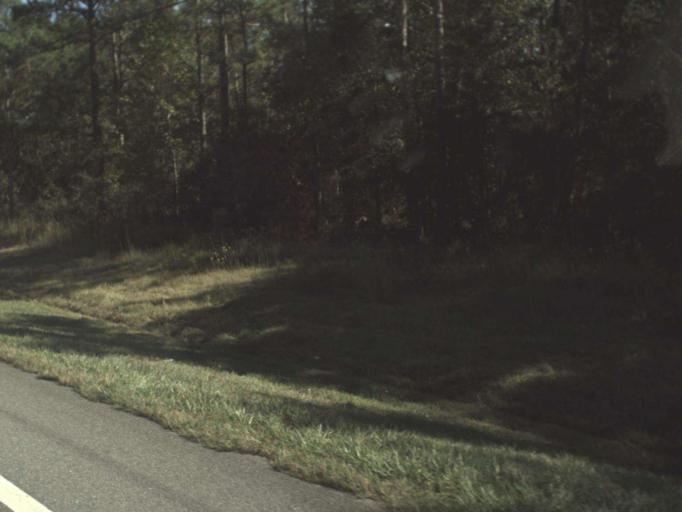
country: US
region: Florida
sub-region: Walton County
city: Freeport
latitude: 30.4795
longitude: -86.0822
